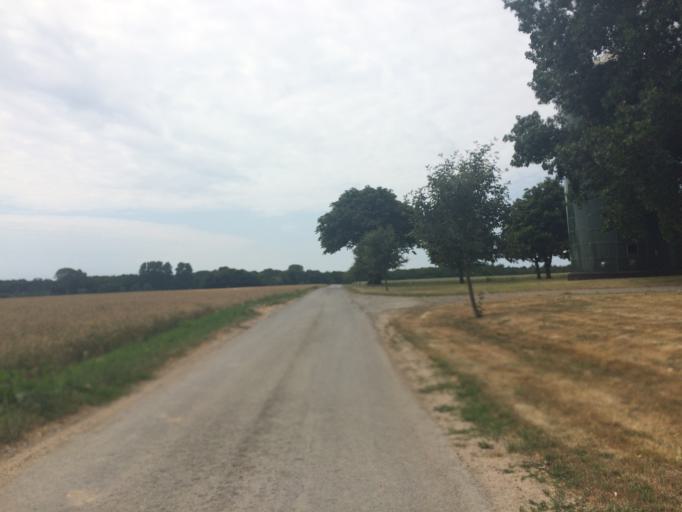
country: DK
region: Capital Region
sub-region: Bornholm Kommune
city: Ronne
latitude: 55.1758
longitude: 14.7288
